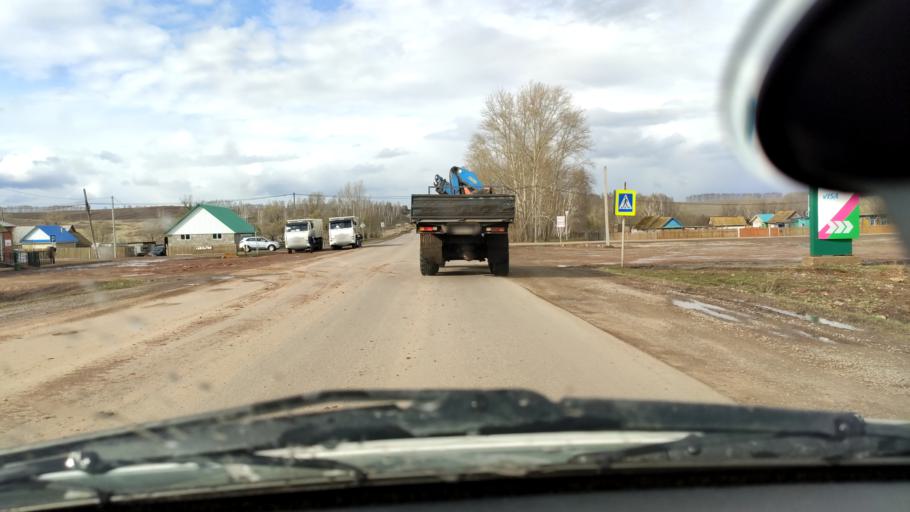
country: RU
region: Bashkortostan
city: Buzdyak
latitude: 54.6871
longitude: 54.5550
